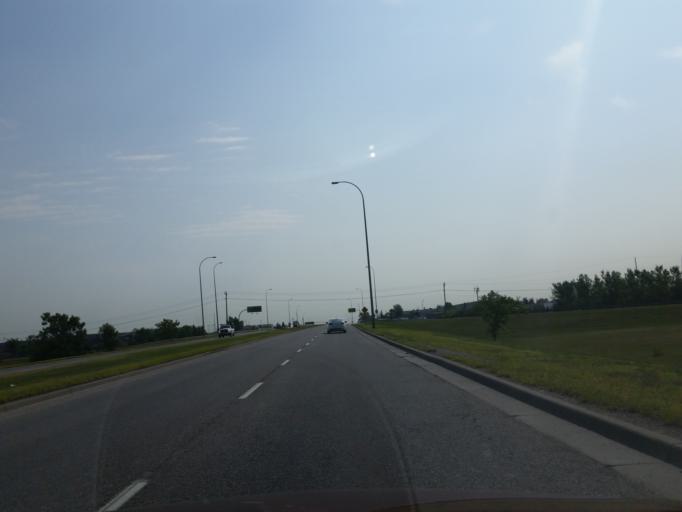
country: CA
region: Alberta
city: Calgary
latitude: 51.0668
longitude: -114.0061
